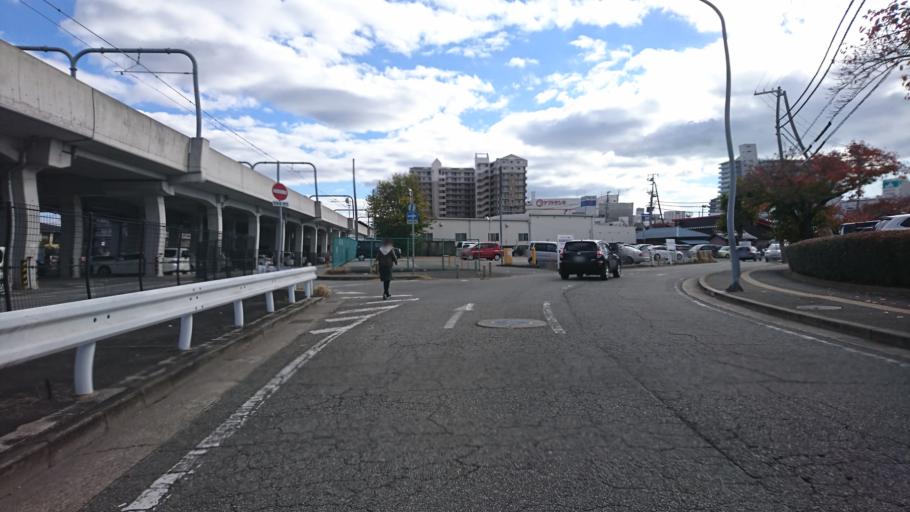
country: JP
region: Hyogo
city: Kakogawacho-honmachi
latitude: 34.7697
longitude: 134.8370
